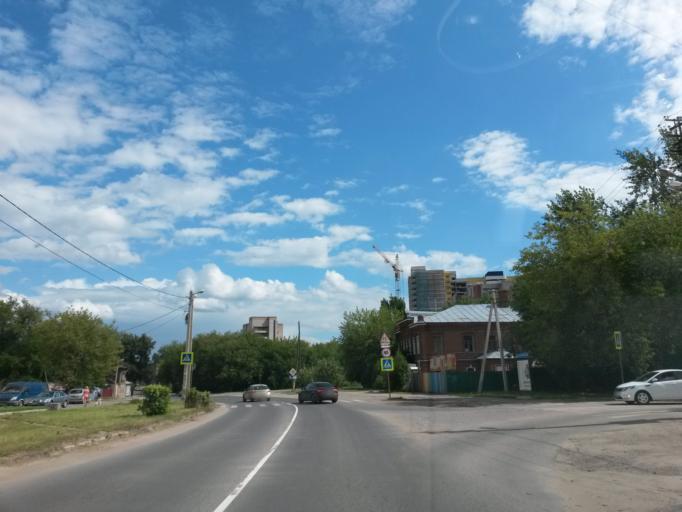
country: RU
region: Ivanovo
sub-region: Gorod Ivanovo
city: Ivanovo
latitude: 56.9890
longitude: 40.9752
